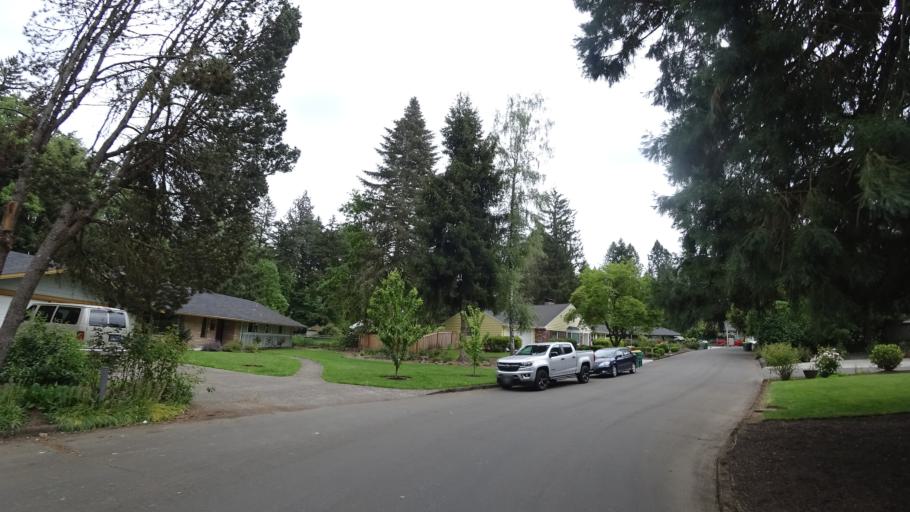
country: US
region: Oregon
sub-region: Washington County
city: Raleigh Hills
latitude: 45.4699
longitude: -122.7747
